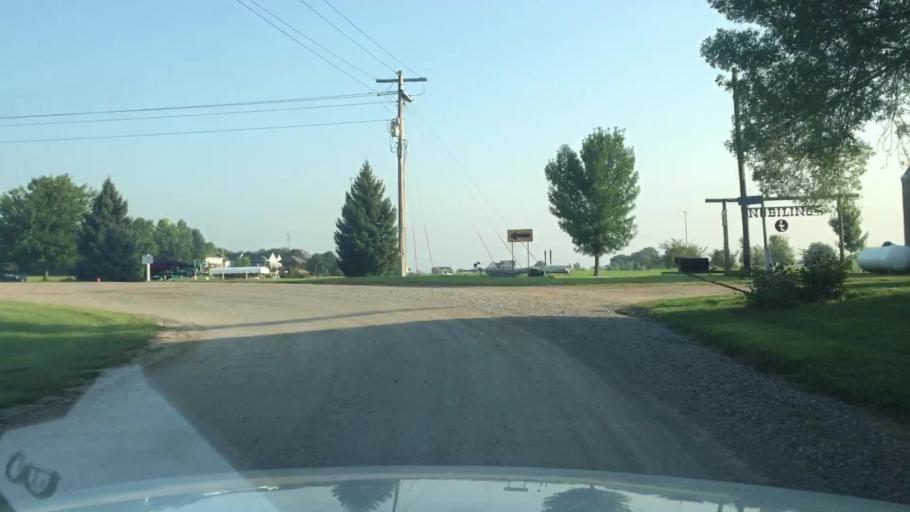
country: US
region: Iowa
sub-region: Story County
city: Huxley
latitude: 41.9112
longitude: -93.5746
